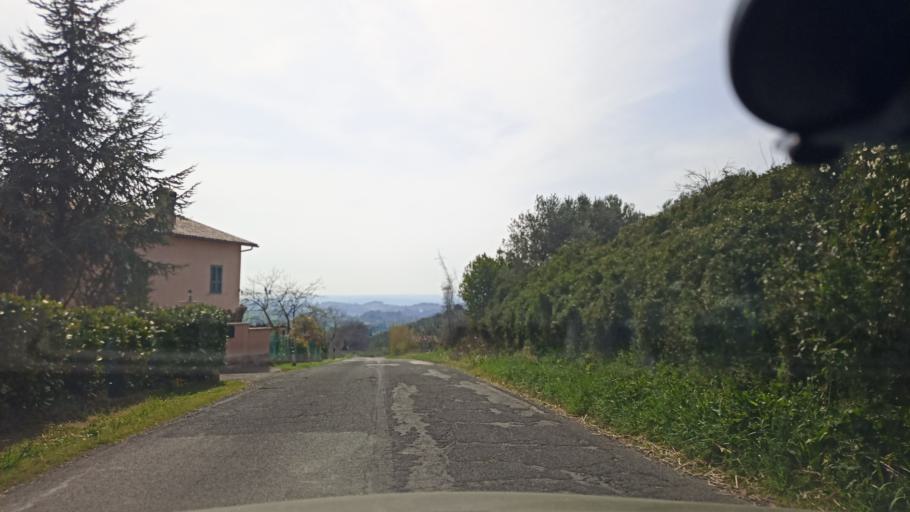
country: IT
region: Latium
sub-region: Provincia di Rieti
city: Torri in Sabina
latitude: 42.3381
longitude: 12.6502
